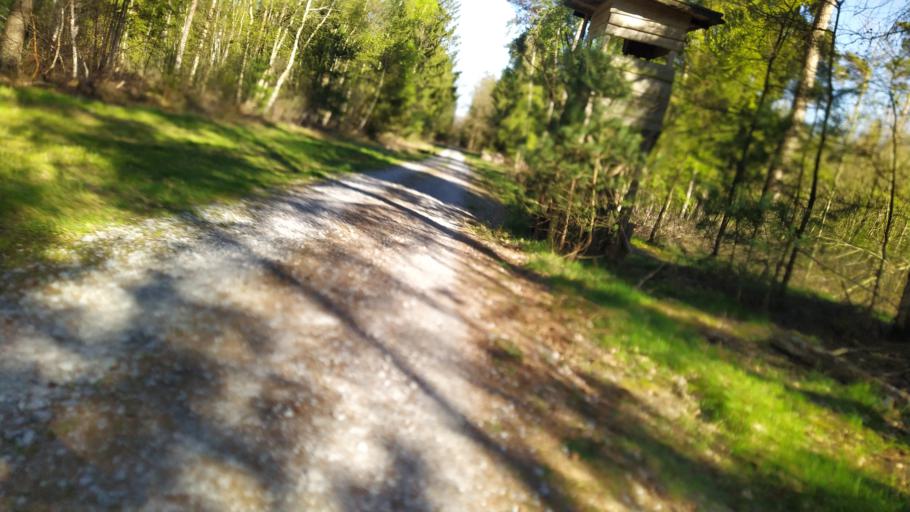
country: DE
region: Lower Saxony
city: Klein Meckelsen
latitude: 53.2934
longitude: 9.4753
